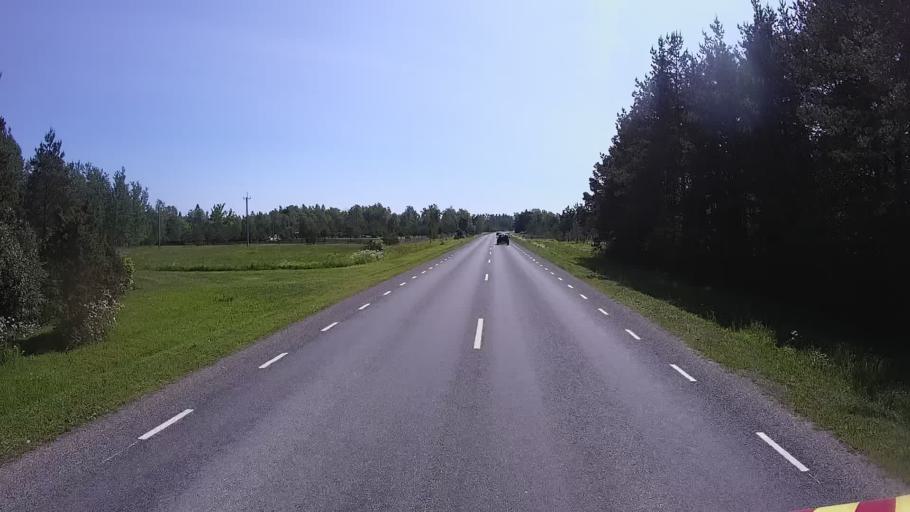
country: EE
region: Saare
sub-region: Kuressaare linn
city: Kuressaare
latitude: 58.3110
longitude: 22.4614
